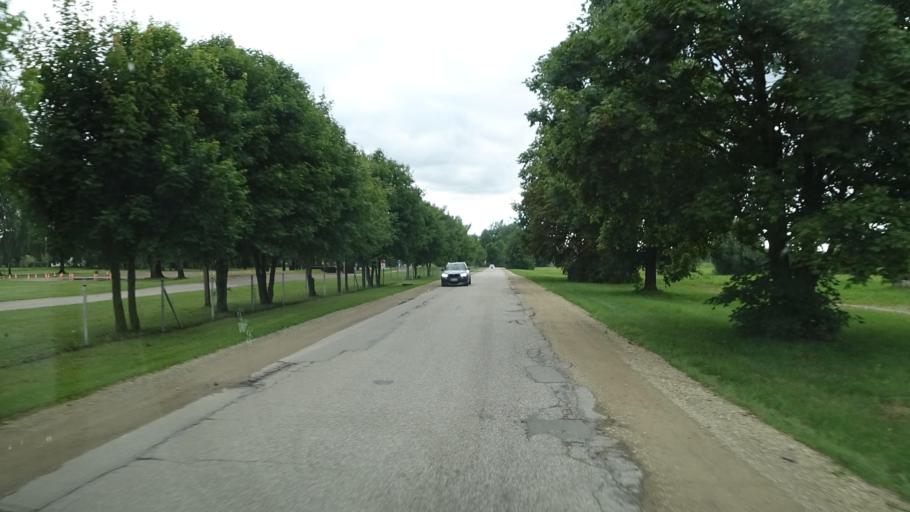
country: LT
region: Marijampoles apskritis
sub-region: Marijampole Municipality
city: Marijampole
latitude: 54.5817
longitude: 23.3686
